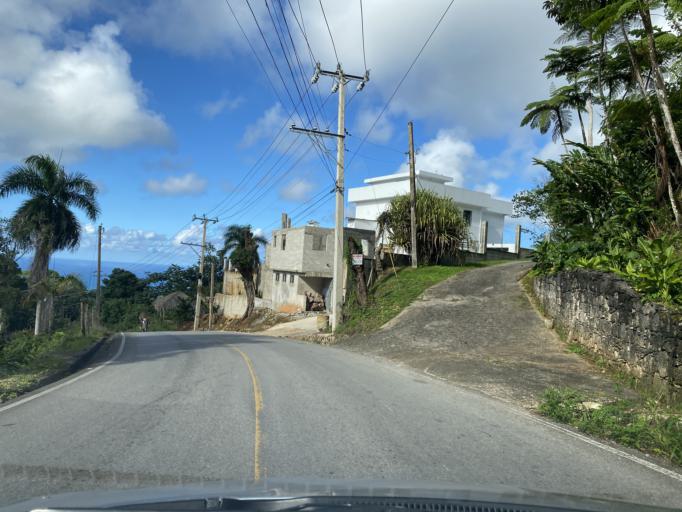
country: DO
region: Samana
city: Las Terrenas
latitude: 19.2747
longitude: -69.5501
